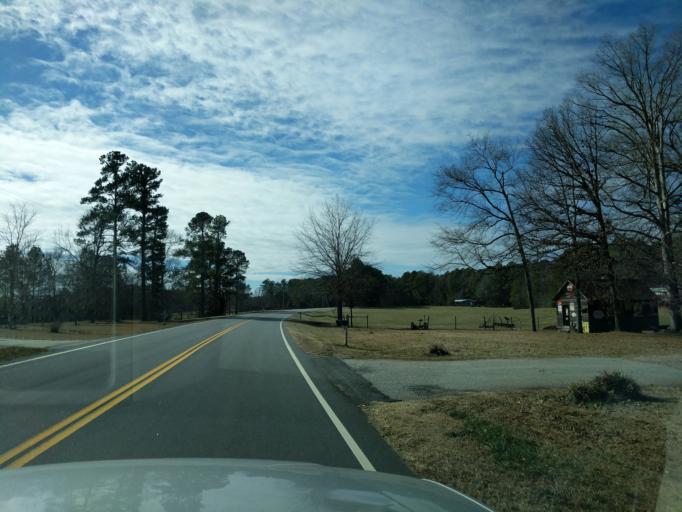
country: US
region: South Carolina
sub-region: Saluda County
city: Saluda
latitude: 33.9544
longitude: -81.9025
